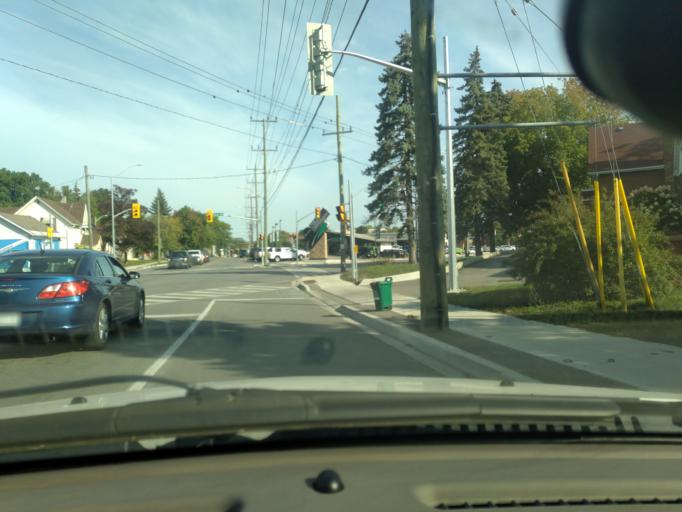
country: CA
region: Ontario
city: Barrie
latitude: 44.3702
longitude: -79.6931
